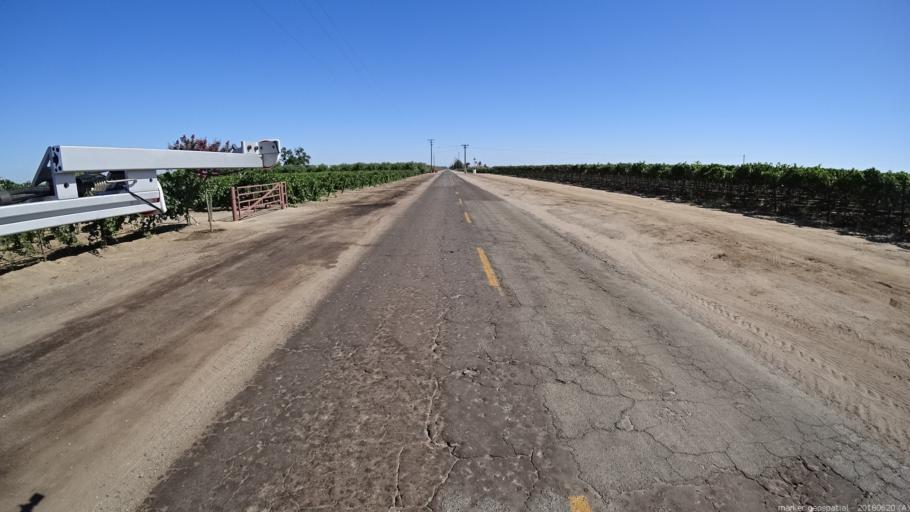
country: US
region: California
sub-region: Madera County
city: Parkwood
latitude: 36.8647
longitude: -120.0374
